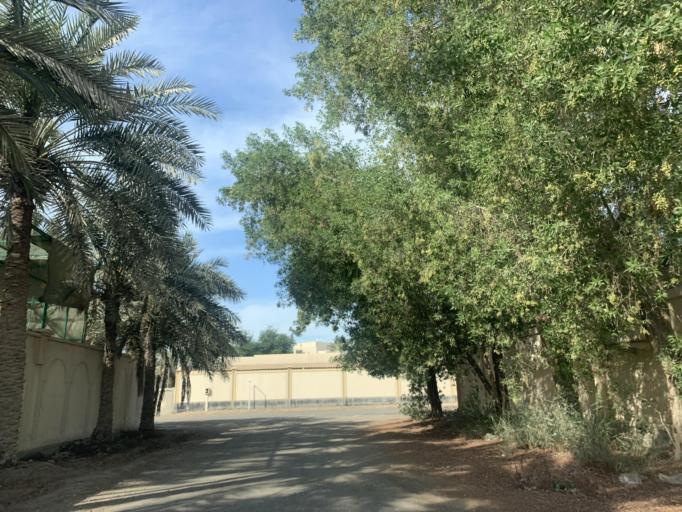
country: BH
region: Central Governorate
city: Madinat Hamad
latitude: 26.1229
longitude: 50.4674
